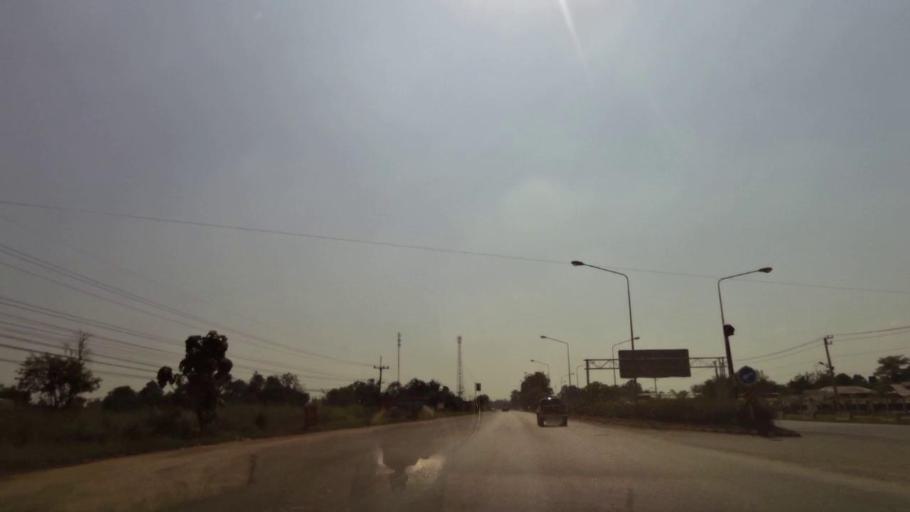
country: TH
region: Phichit
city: Wachira Barami
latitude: 16.3491
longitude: 100.1286
